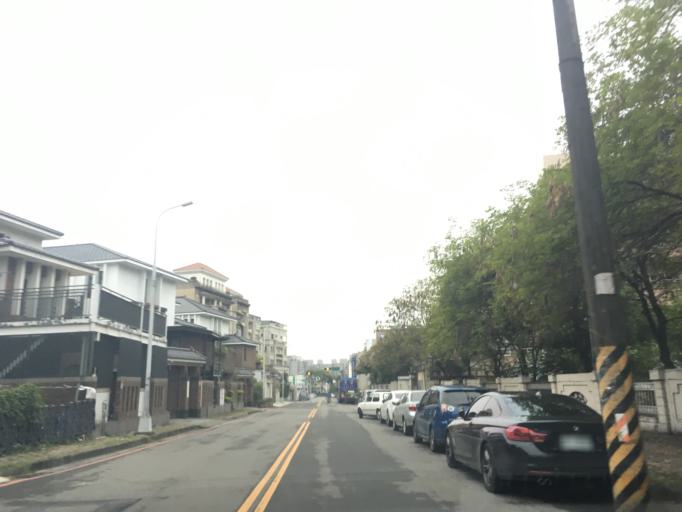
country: TW
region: Taiwan
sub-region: Taichung City
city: Taichung
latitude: 24.1670
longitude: 120.7134
